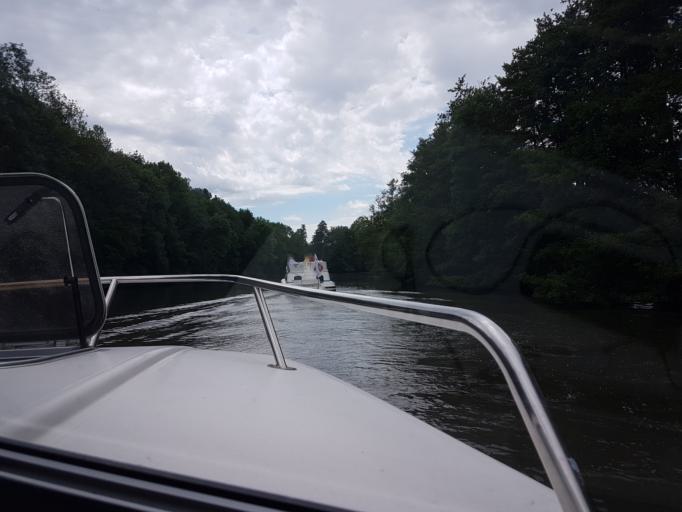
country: FR
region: Bourgogne
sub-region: Departement de la Nievre
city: Clamecy
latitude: 47.4670
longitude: 3.5282
